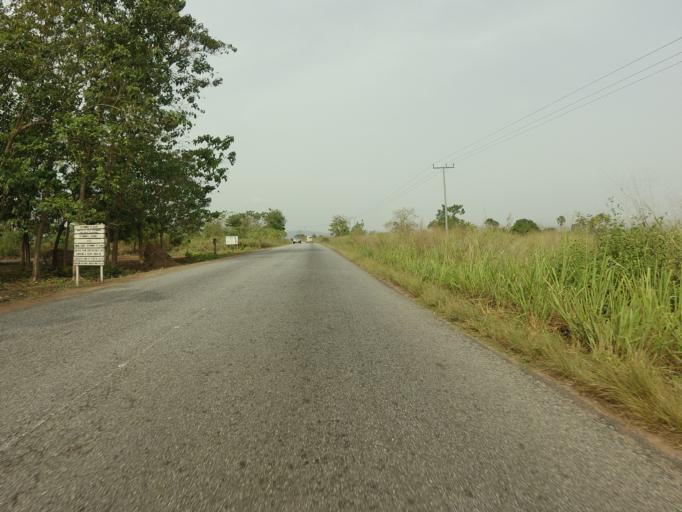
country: GH
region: Volta
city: Ho
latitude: 6.5732
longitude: 0.3609
